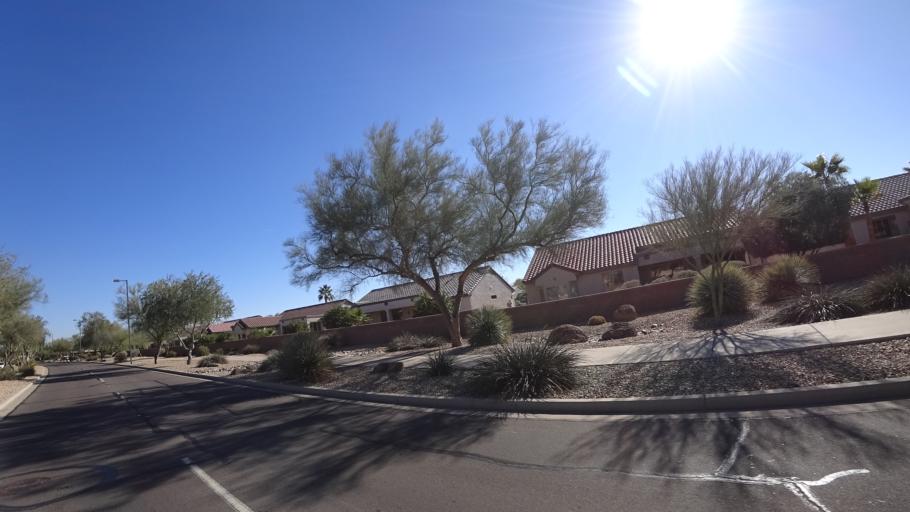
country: US
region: Arizona
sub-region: Maricopa County
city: Sun City West
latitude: 33.6697
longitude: -112.4077
